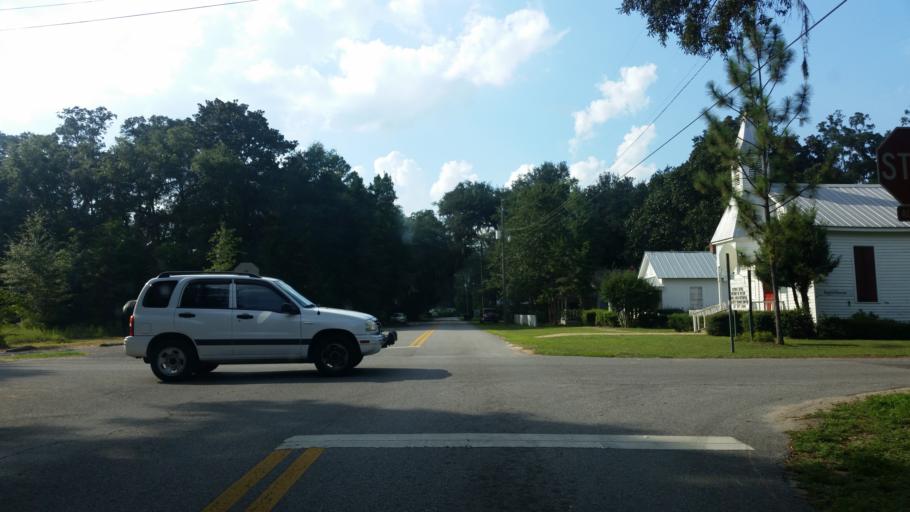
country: US
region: Florida
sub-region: Santa Rosa County
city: Bagdad
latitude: 30.5984
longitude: -87.0321
